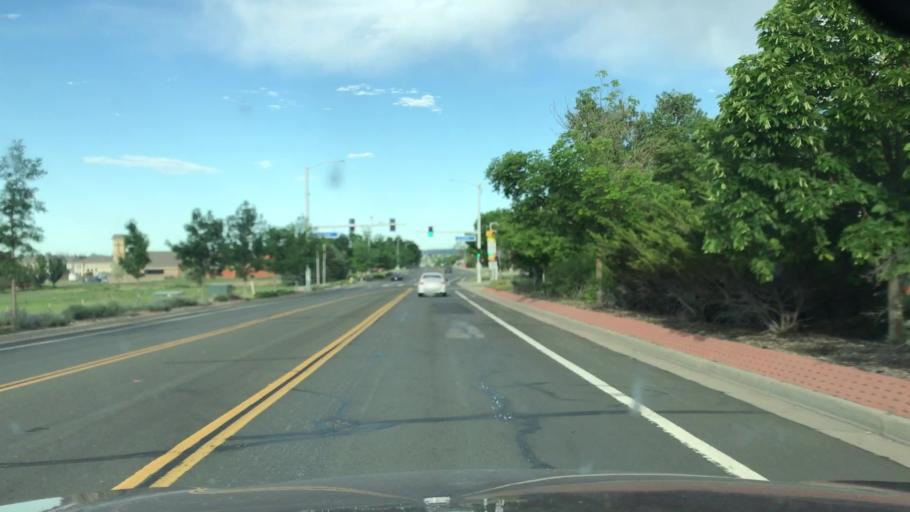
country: US
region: Colorado
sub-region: Broomfield County
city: Broomfield
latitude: 39.9432
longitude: -105.0590
